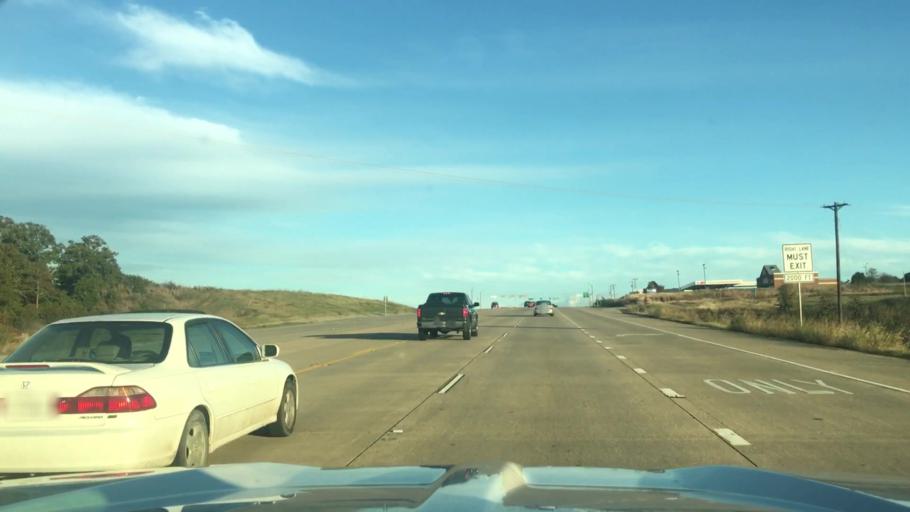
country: US
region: Texas
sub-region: Denton County
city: Cross Roads
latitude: 33.2362
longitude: -97.0193
